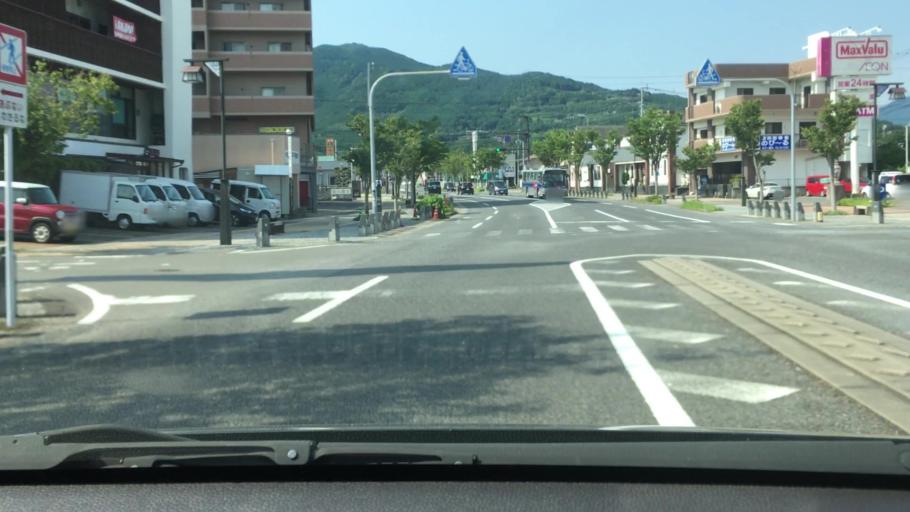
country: JP
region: Saga Prefecture
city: Imaricho-ko
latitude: 33.2714
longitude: 129.8765
